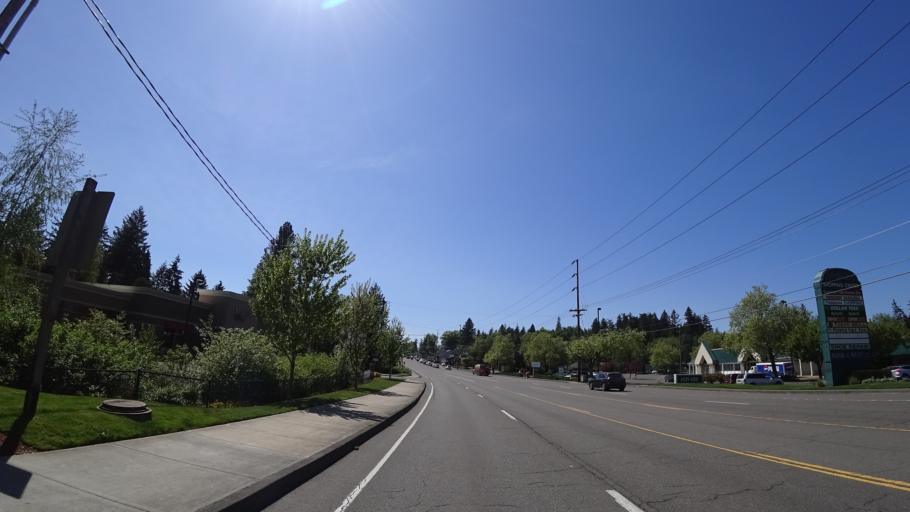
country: US
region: Oregon
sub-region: Washington County
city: Raleigh Hills
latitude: 45.4870
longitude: -122.7448
